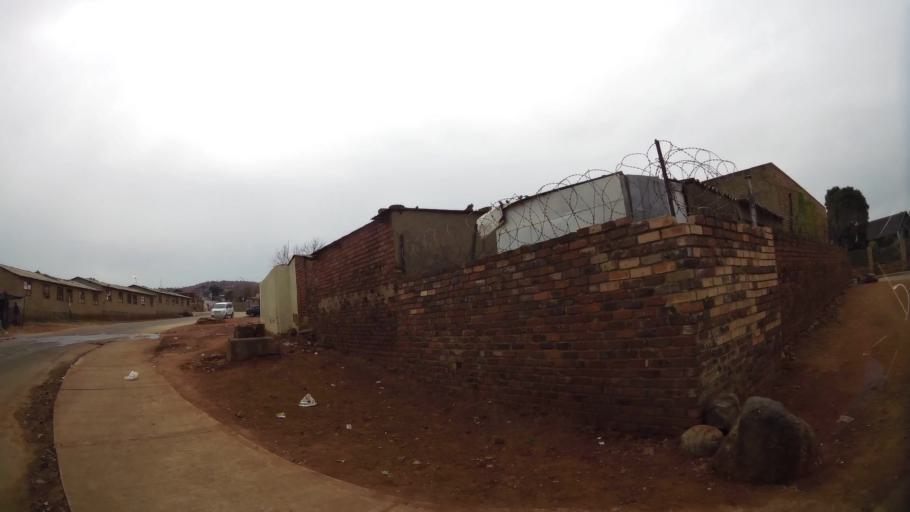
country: ZA
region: Gauteng
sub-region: City of Tshwane Metropolitan Municipality
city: Pretoria
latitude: -25.7030
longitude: 28.3296
